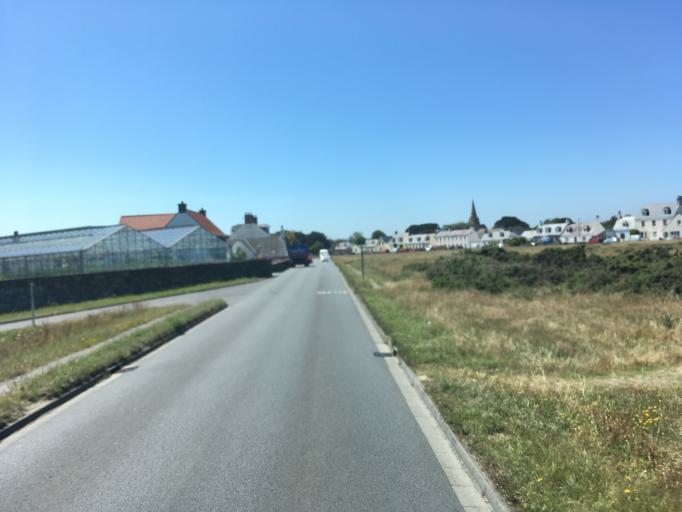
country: GG
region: St Peter Port
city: Saint Peter Port
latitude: 49.4959
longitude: -2.5360
